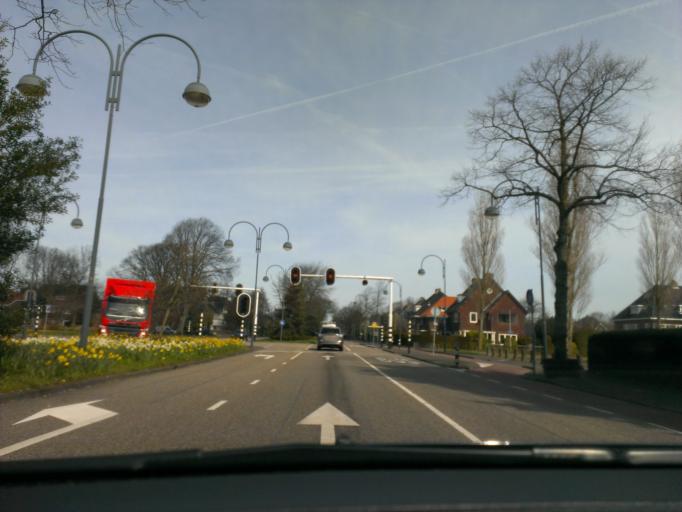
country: NL
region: North Holland
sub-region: Gemeente Heemstede
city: Heemstede
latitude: 52.3523
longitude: 4.6246
